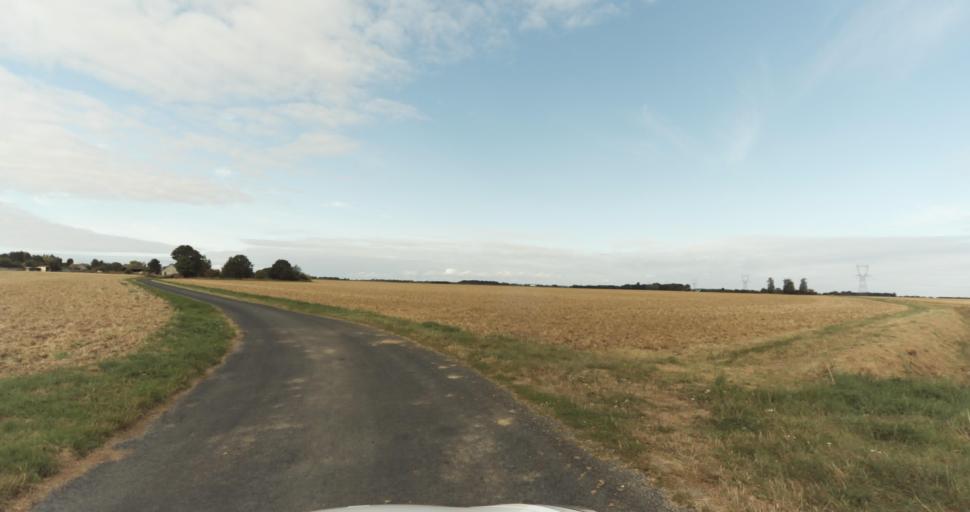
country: FR
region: Haute-Normandie
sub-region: Departement de l'Eure
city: La Madeleine-de-Nonancourt
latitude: 48.8466
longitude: 1.1970
